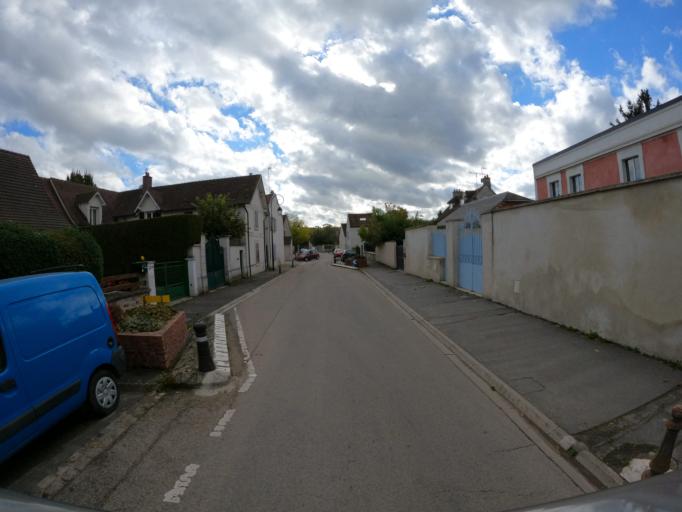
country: FR
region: Ile-de-France
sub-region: Departement de Seine-et-Marne
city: Chalifert
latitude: 48.9061
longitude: 2.7782
